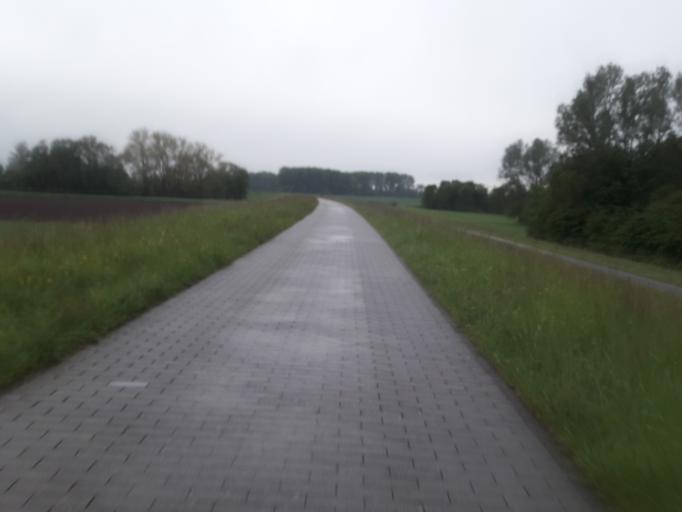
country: DE
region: North Rhine-Westphalia
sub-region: Regierungsbezirk Dusseldorf
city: Meerbusch
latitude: 51.2763
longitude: 6.6982
